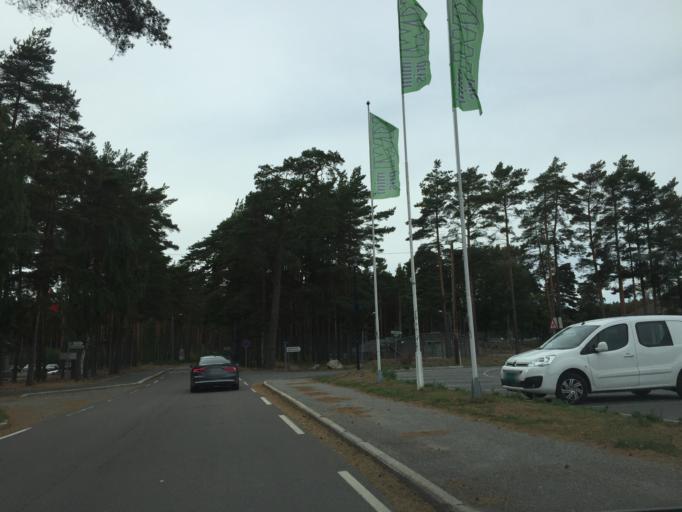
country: NO
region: Ostfold
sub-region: Hvaler
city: Skjaerhalden
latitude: 59.0280
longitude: 11.0325
